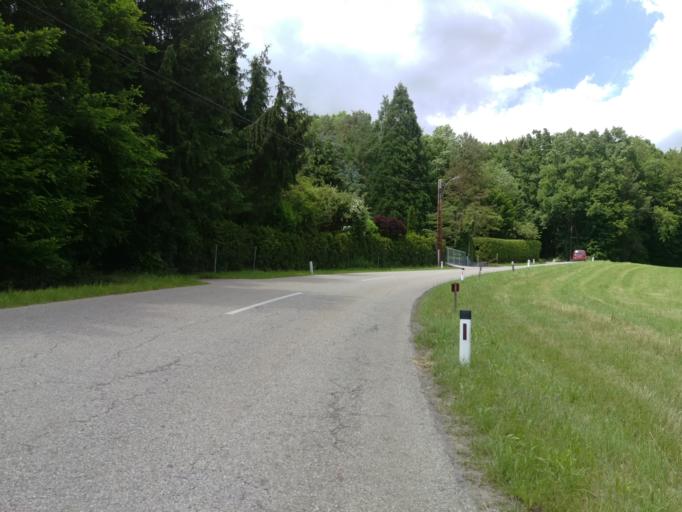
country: AT
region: Styria
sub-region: Graz Stadt
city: Mariatrost
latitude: 47.1026
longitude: 15.5094
